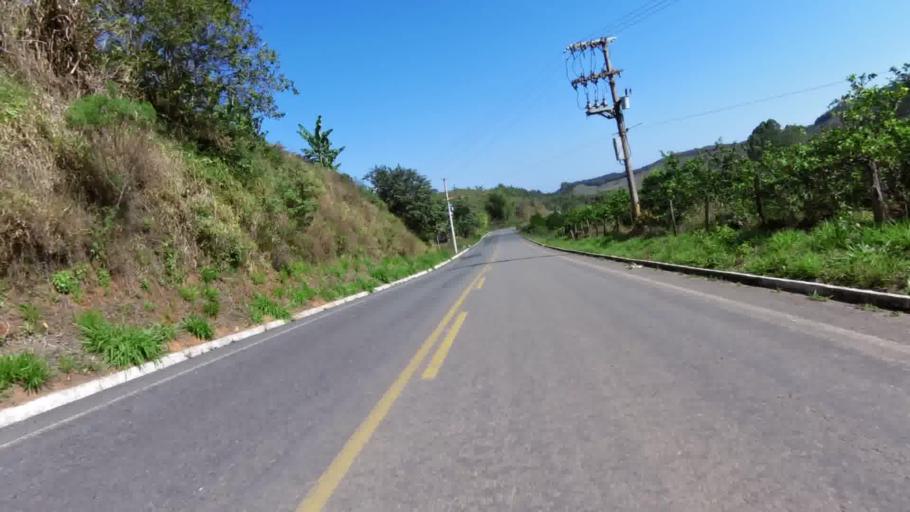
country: BR
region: Espirito Santo
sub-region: Alfredo Chaves
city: Alfredo Chaves
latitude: -20.5246
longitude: -40.7785
